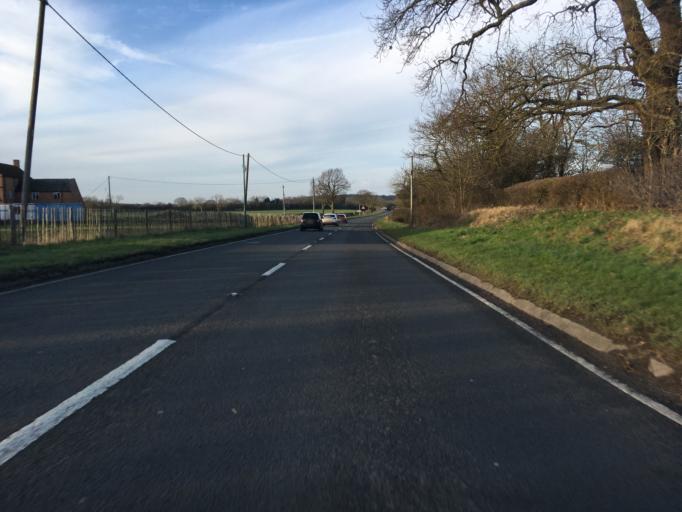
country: GB
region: England
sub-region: Warwickshire
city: Henley in Arden
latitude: 52.2393
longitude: -1.7451
